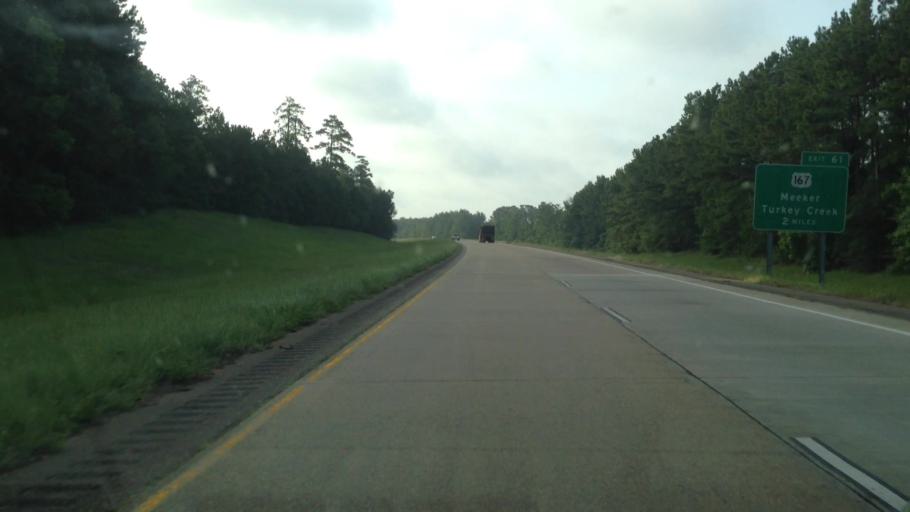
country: US
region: Louisiana
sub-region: Rapides Parish
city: Lecompte
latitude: 31.0315
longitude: -92.4095
